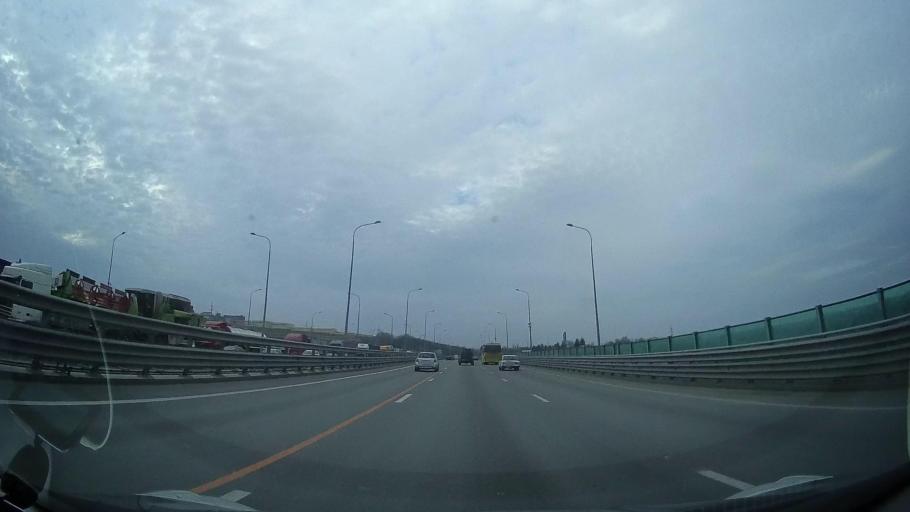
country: RU
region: Rostov
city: Aksay
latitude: 47.2410
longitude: 39.8527
